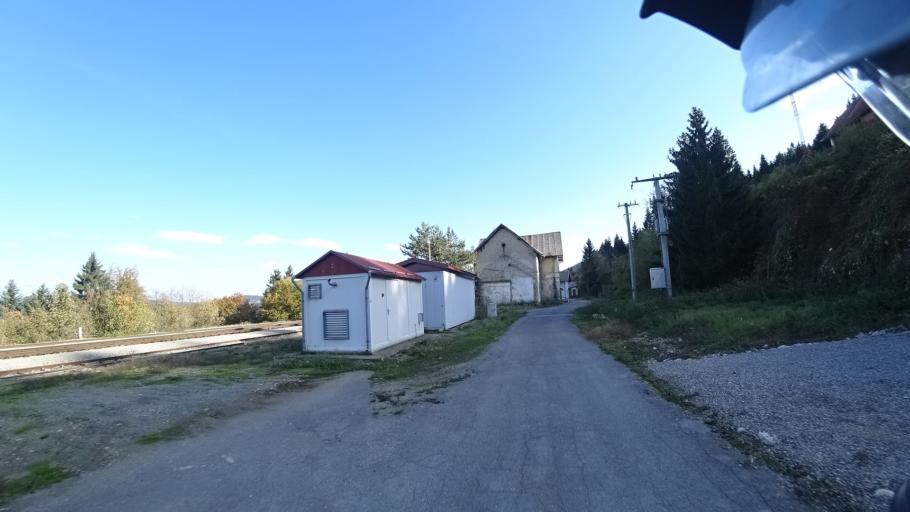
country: HR
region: Karlovacka
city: Plaski
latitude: 44.9780
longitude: 15.4292
